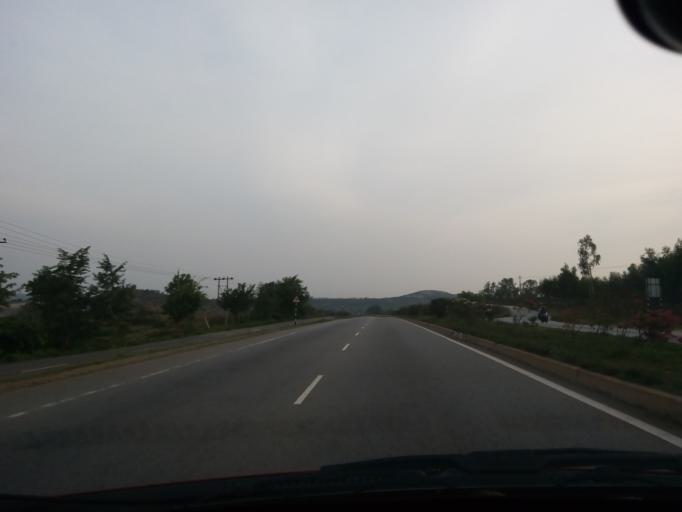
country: IN
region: Karnataka
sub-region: Chikkaballapur
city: Chik Ballapur
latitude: 13.5293
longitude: 77.7653
